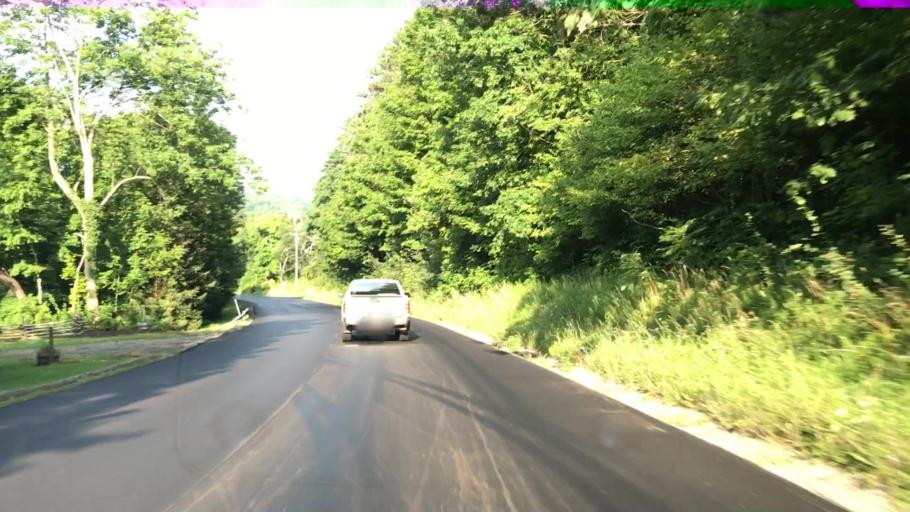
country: US
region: New York
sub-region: Chautauqua County
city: Brocton
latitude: 42.3187
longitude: -79.3514
